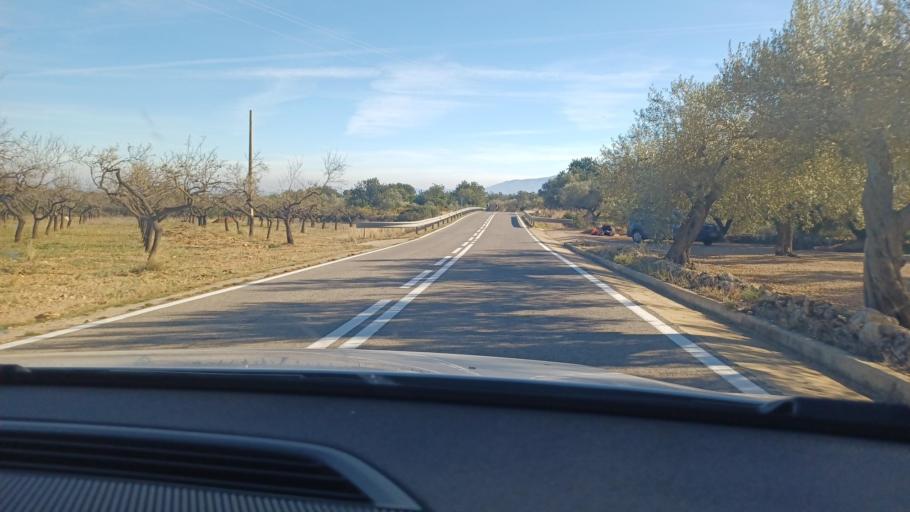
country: ES
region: Catalonia
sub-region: Provincia de Tarragona
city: Mas de Barberans
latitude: 40.7281
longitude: 0.3820
